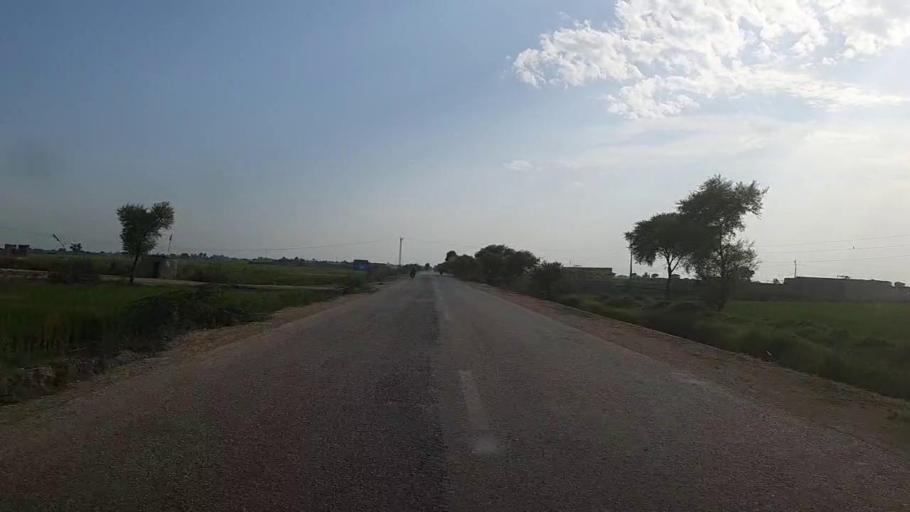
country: PK
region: Sindh
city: Thul
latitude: 28.2054
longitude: 68.7451
